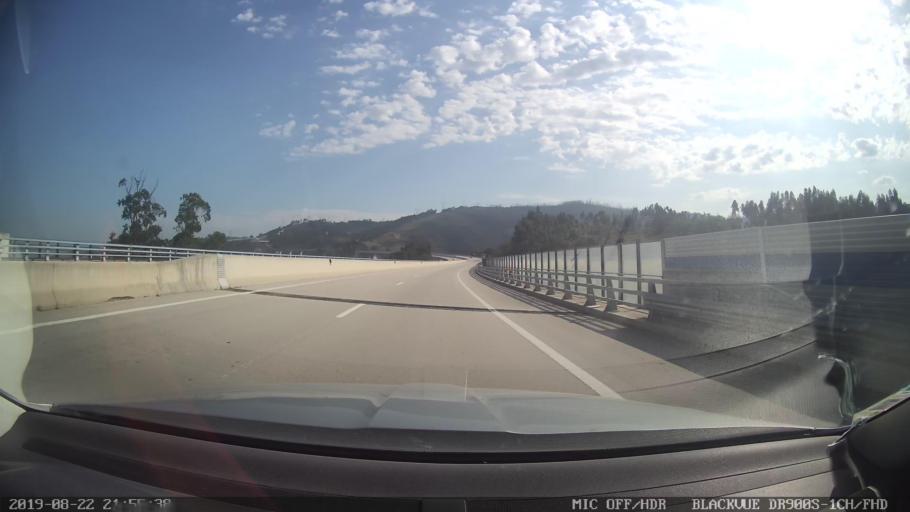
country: PT
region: Coimbra
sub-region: Coimbra
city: Coimbra
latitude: 40.1571
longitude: -8.3843
